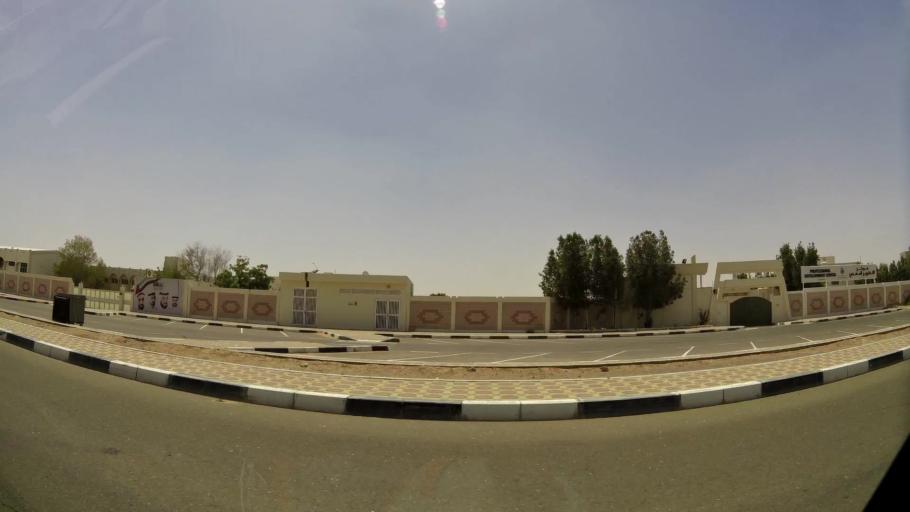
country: AE
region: Abu Dhabi
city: Al Ain
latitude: 24.2593
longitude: 55.7037
